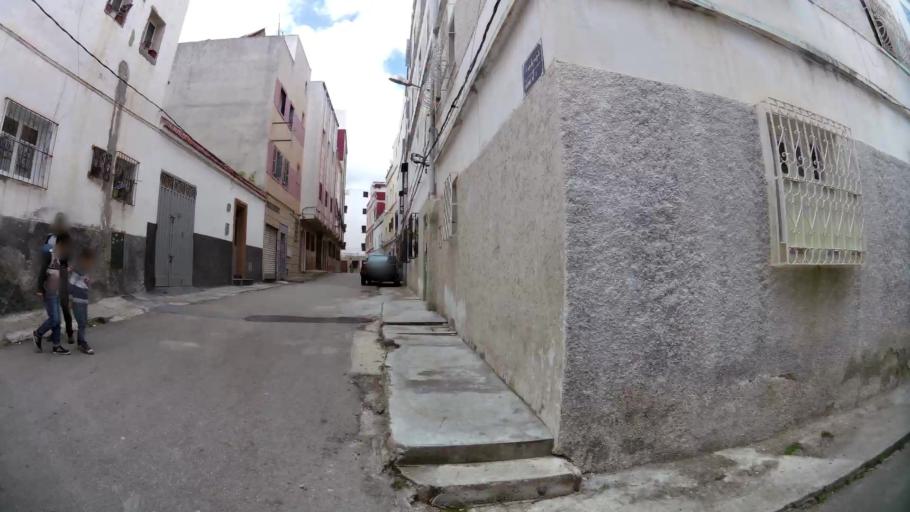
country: MA
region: Tanger-Tetouan
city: Tetouan
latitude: 35.5760
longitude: -5.3526
